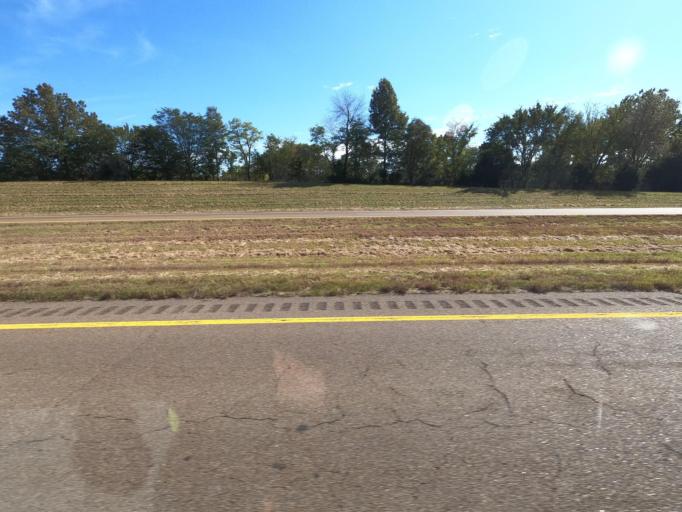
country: US
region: Tennessee
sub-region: Obion County
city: South Fulton
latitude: 36.4888
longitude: -88.9273
